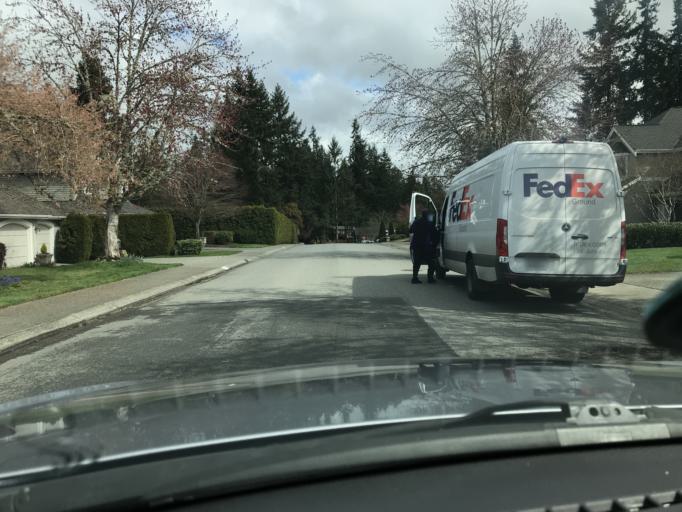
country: US
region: Washington
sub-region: King County
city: City of Sammamish
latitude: 47.5789
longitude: -122.0529
